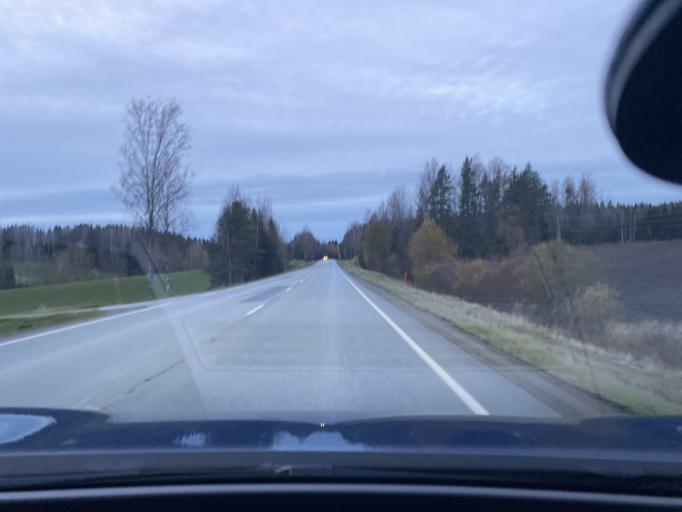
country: FI
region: Uusimaa
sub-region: Helsinki
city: Sammatti
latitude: 60.3878
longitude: 23.8247
